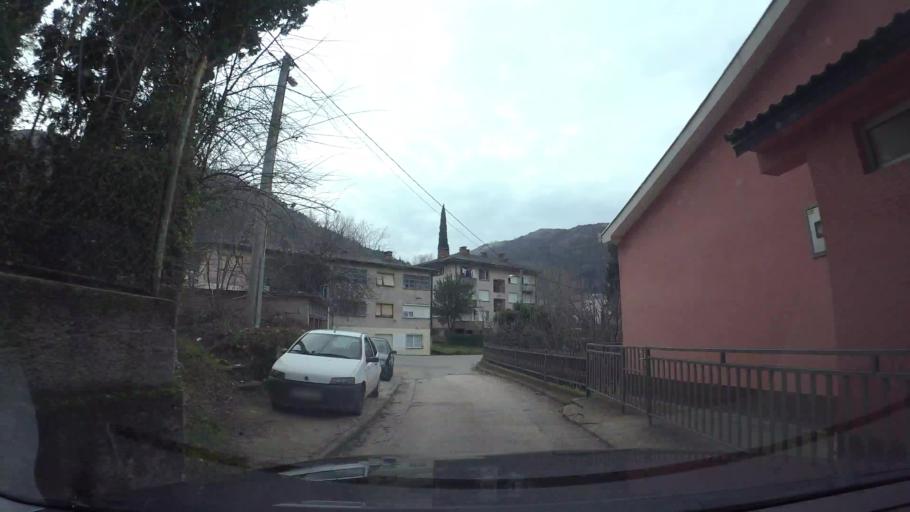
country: BA
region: Federation of Bosnia and Herzegovina
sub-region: Hercegovacko-Bosanski Kanton
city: Mostar
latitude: 43.3362
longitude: 17.7988
